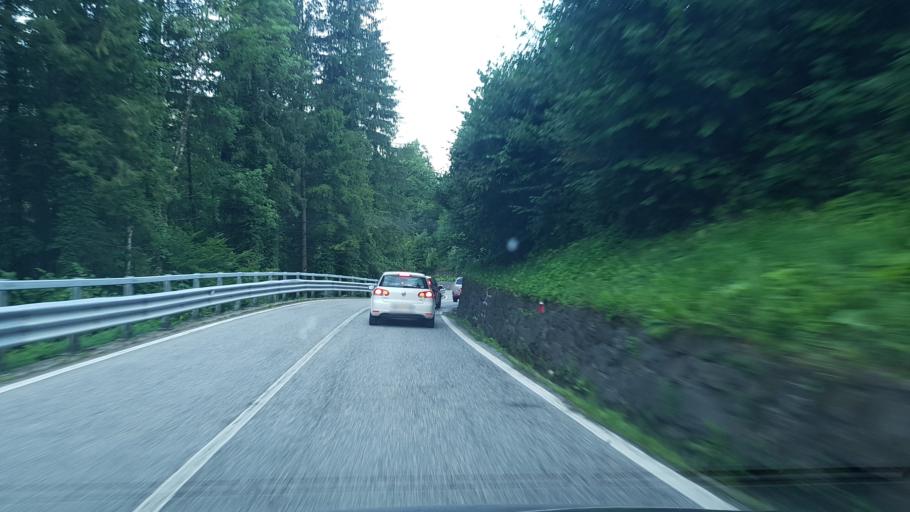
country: IT
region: Friuli Venezia Giulia
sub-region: Provincia di Udine
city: Comeglians
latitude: 46.5300
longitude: 12.8689
